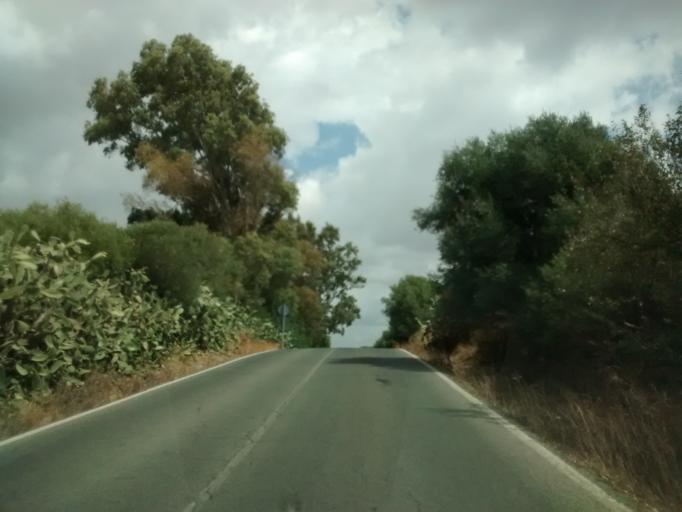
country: ES
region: Andalusia
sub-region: Provincia de Cadiz
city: Medina Sidonia
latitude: 36.4798
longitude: -5.9150
